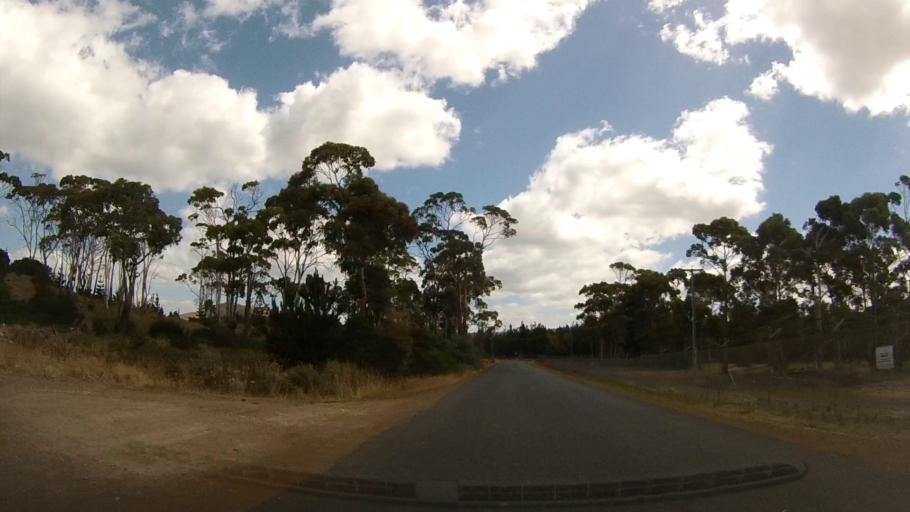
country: AU
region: Tasmania
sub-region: Clarence
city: Seven Mile Beach
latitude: -42.8480
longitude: 147.5234
